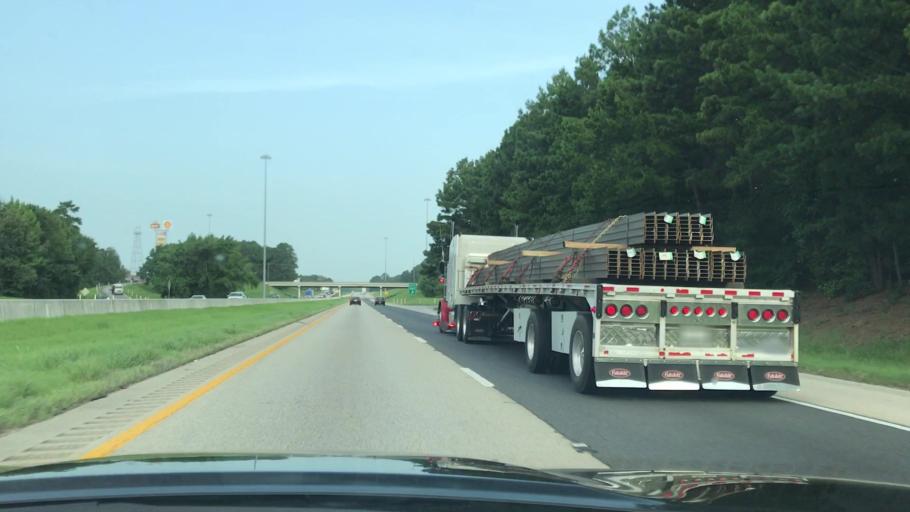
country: US
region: Texas
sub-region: Gregg County
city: Kilgore
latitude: 32.4331
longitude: -94.8578
